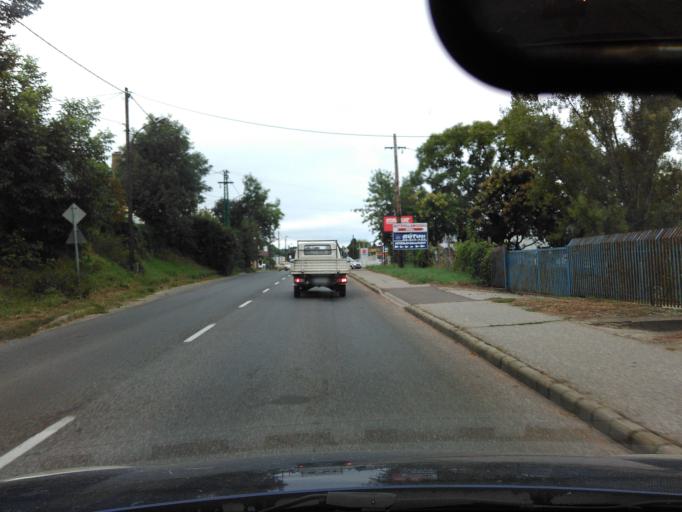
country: HU
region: Nograd
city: Salgotarjan
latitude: 48.0856
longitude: 19.7934
